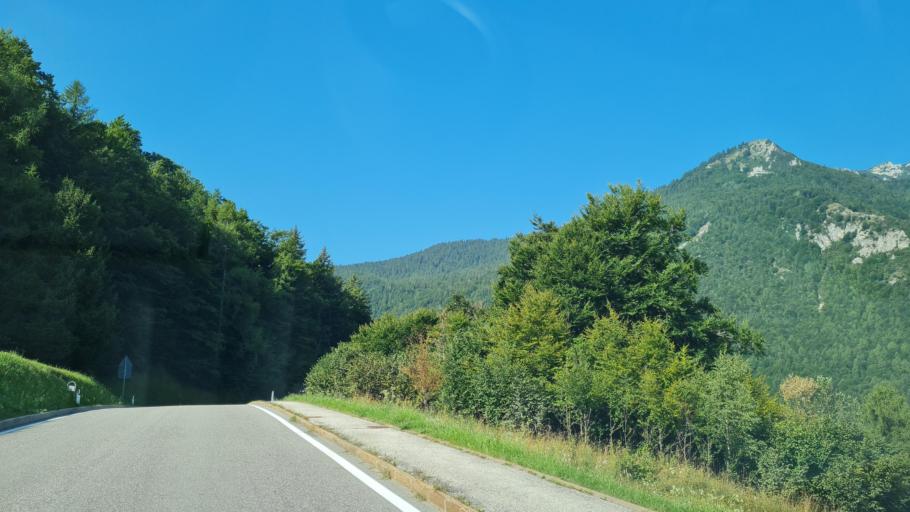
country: IT
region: Trentino-Alto Adige
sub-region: Provincia di Trento
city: Centa San Nicolo
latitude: 45.9381
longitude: 11.2285
